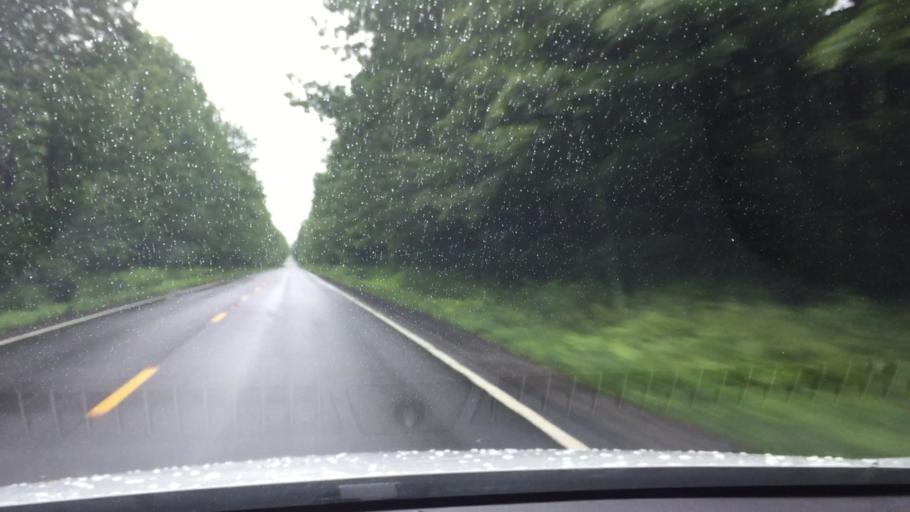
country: US
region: Massachusetts
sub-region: Berkshire County
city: Hinsdale
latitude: 42.3783
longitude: -73.1519
